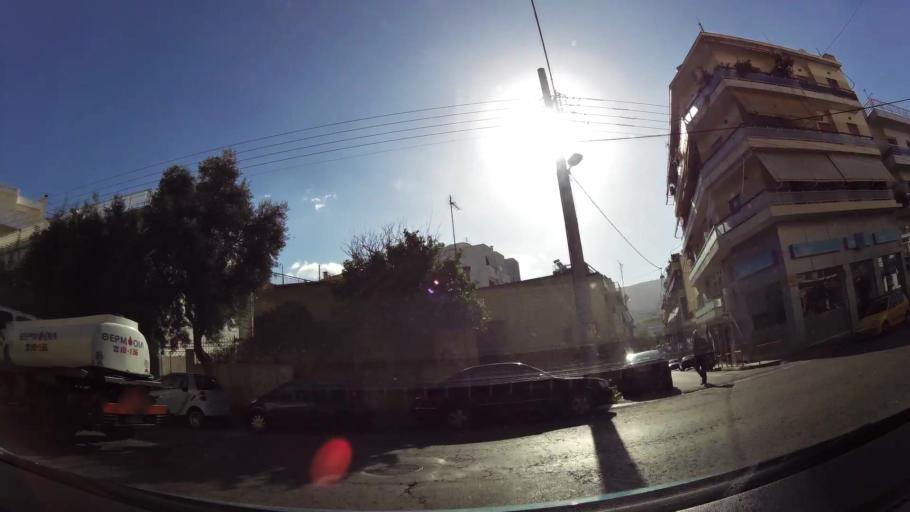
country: GR
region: Attica
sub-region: Nomarchia Athinas
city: Neo Psychiko
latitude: 37.9946
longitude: 23.7758
